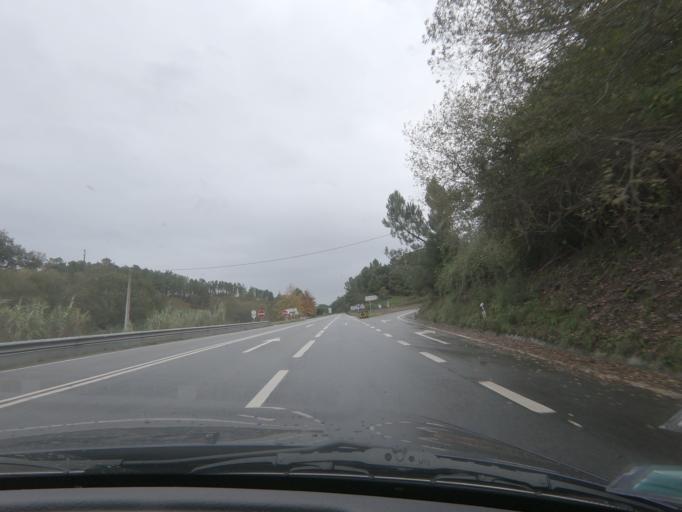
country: PT
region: Porto
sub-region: Amarante
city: Teloes
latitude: 41.3135
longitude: -8.0748
